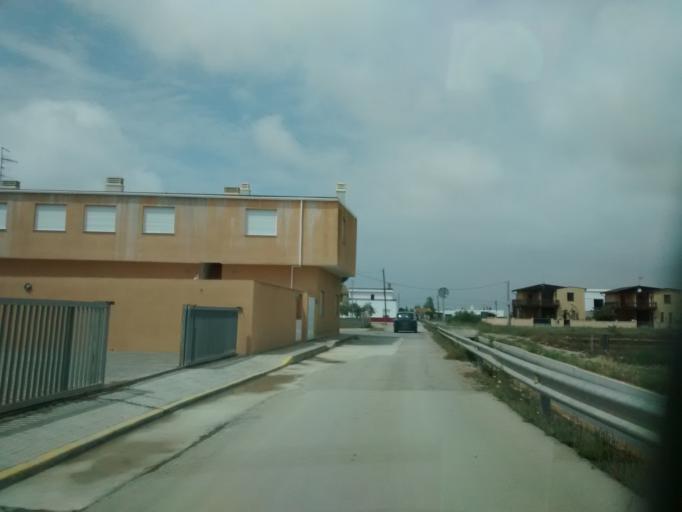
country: ES
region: Catalonia
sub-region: Provincia de Tarragona
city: Deltebre
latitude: 40.6712
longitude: 0.7523
